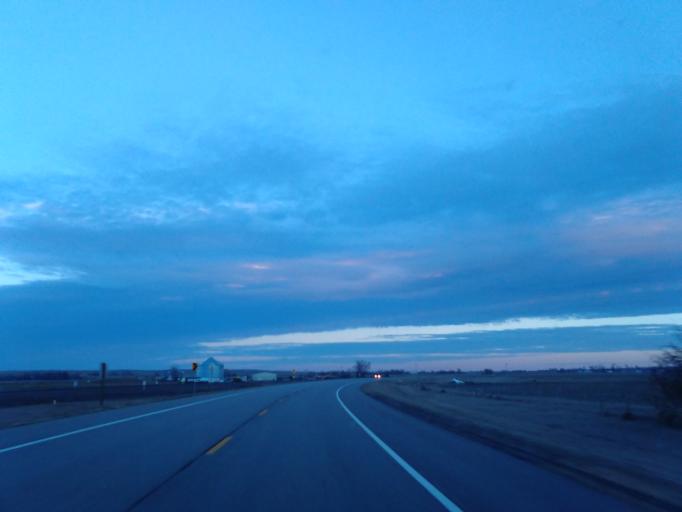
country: US
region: Nebraska
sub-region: Garden County
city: Oshkosh
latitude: 41.4021
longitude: -102.3343
